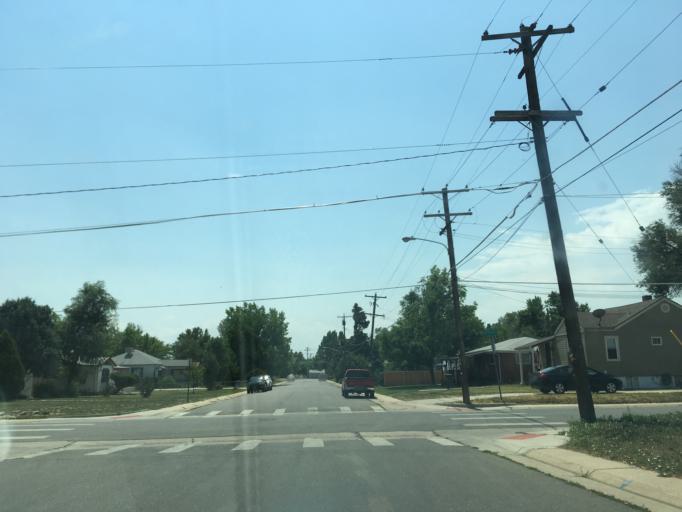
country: US
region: Colorado
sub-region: Arapahoe County
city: Sheridan
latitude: 39.6916
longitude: -105.0321
